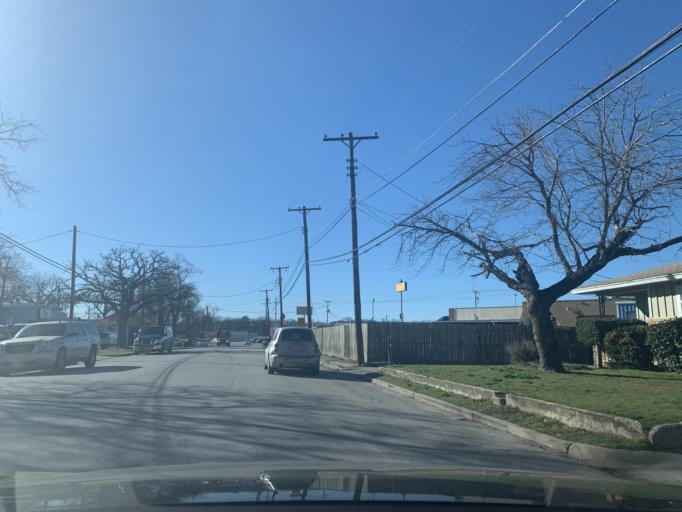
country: US
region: Texas
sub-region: Tarrant County
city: Haltom City
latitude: 32.7818
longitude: -97.2876
